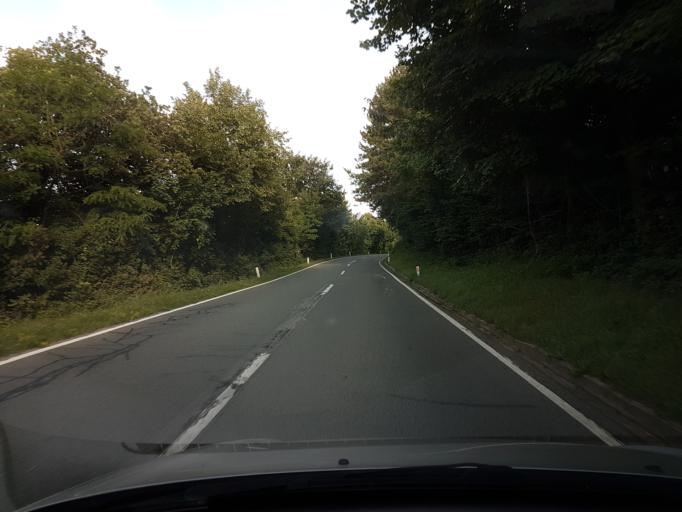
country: SI
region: Sezana
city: Sezana
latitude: 45.7098
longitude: 13.8932
